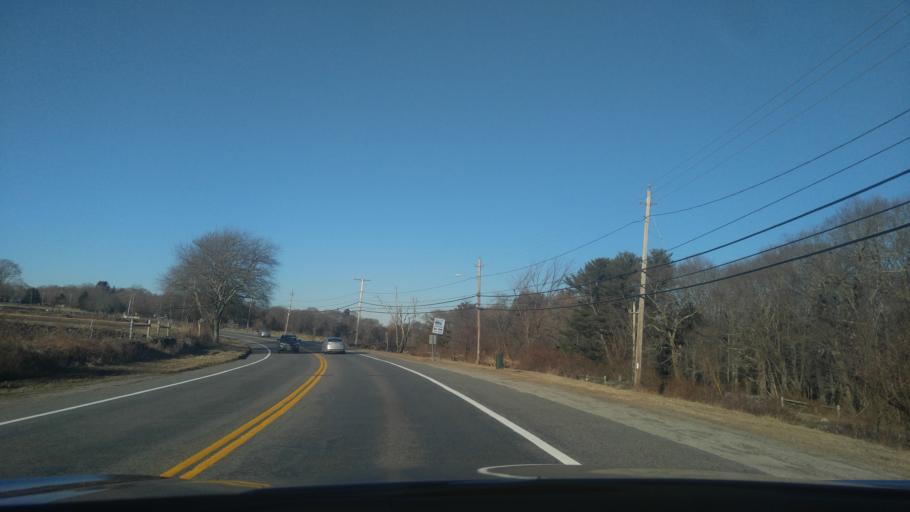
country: US
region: Rhode Island
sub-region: Newport County
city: Jamestown
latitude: 41.5097
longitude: -71.4226
